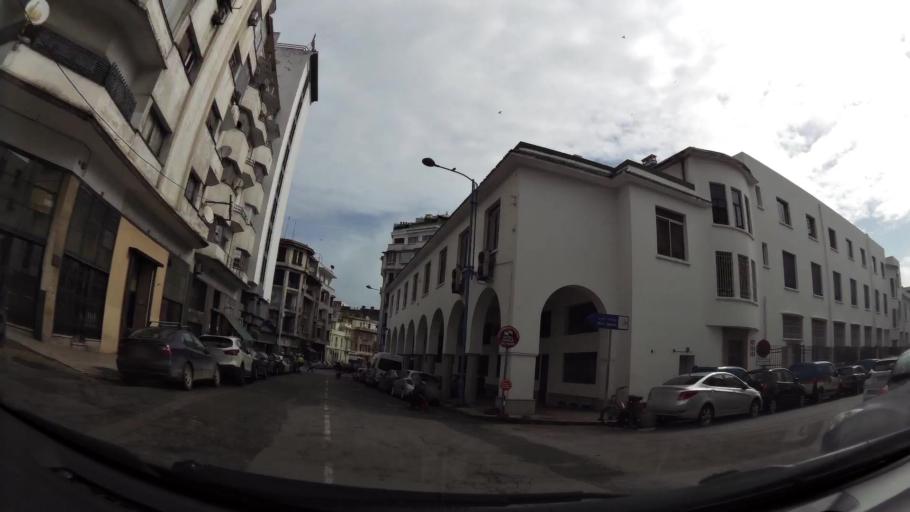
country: MA
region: Grand Casablanca
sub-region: Casablanca
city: Casablanca
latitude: 33.5929
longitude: -7.6204
